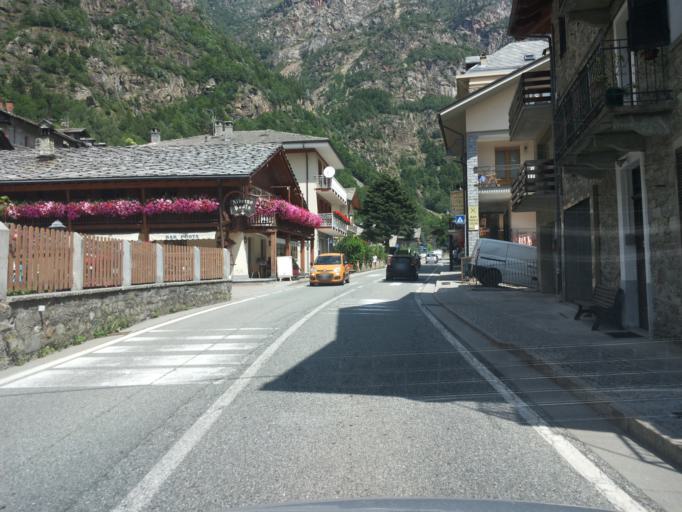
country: IT
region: Aosta Valley
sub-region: Valle d'Aosta
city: Issime
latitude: 45.6855
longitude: 7.8540
